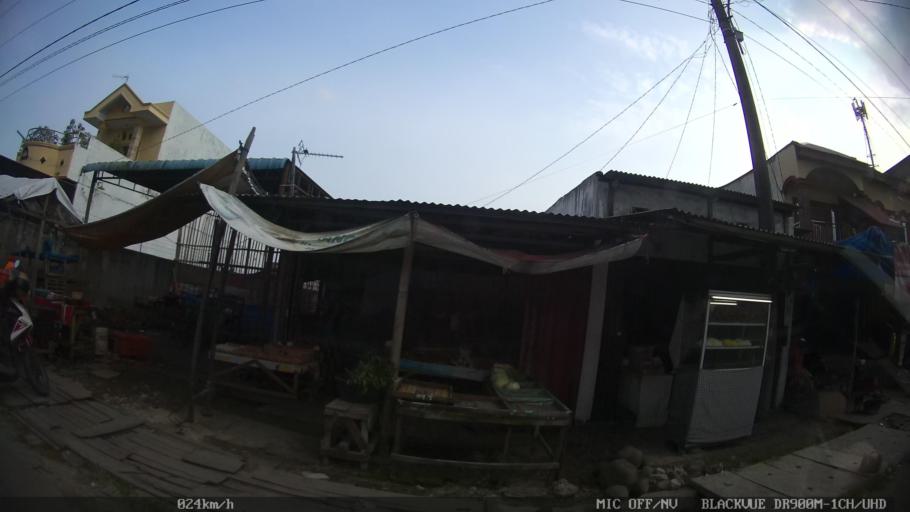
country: ID
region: North Sumatra
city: Medan
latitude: 3.5814
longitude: 98.7315
